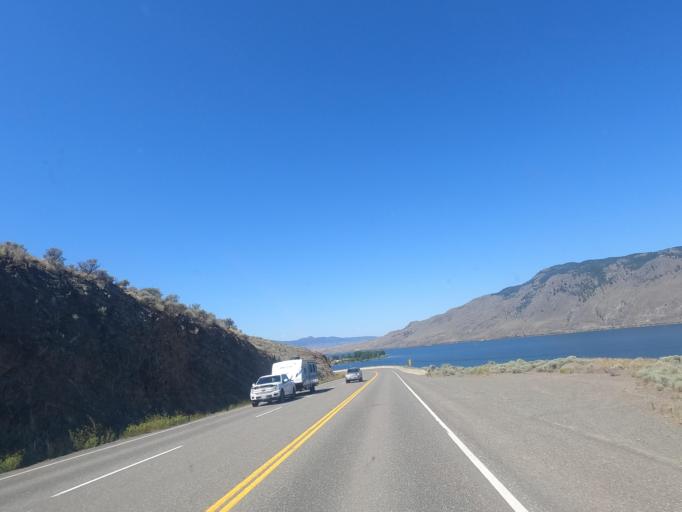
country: CA
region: British Columbia
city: Logan Lake
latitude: 50.7627
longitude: -120.7903
